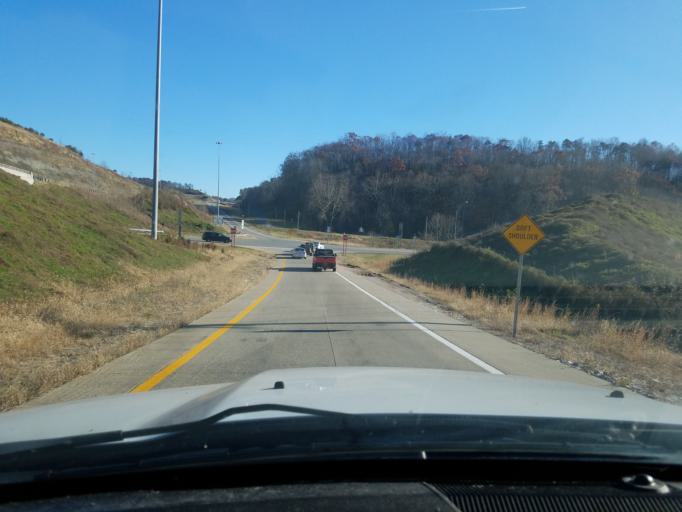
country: US
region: West Virginia
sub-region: Putnam County
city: Teays Valley
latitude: 38.4821
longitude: -81.9289
